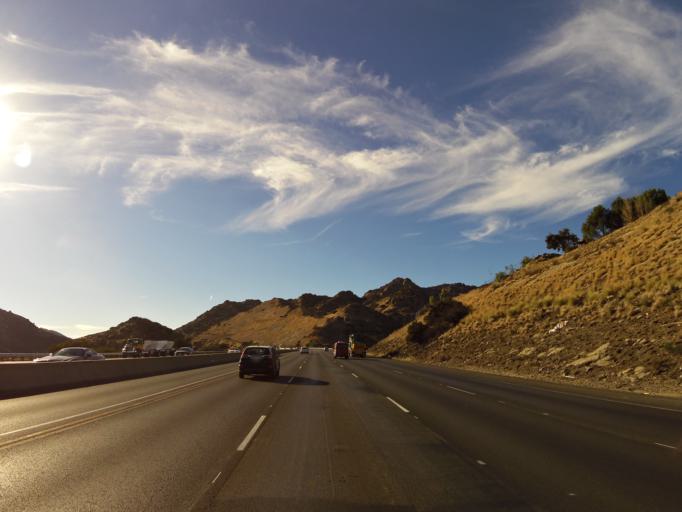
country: US
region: California
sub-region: Los Angeles County
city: Chatsworth
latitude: 34.2763
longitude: -118.6192
